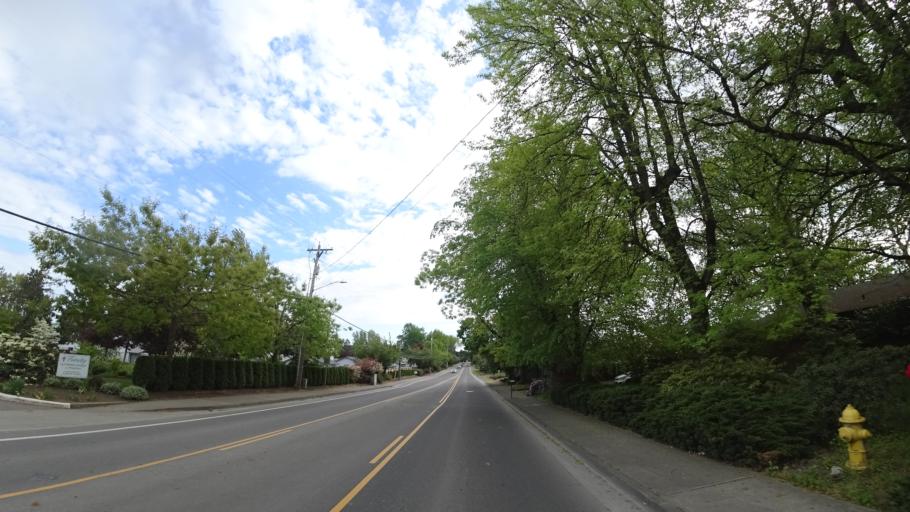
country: US
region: Oregon
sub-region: Washington County
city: Hillsboro
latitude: 45.5030
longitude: -122.9638
